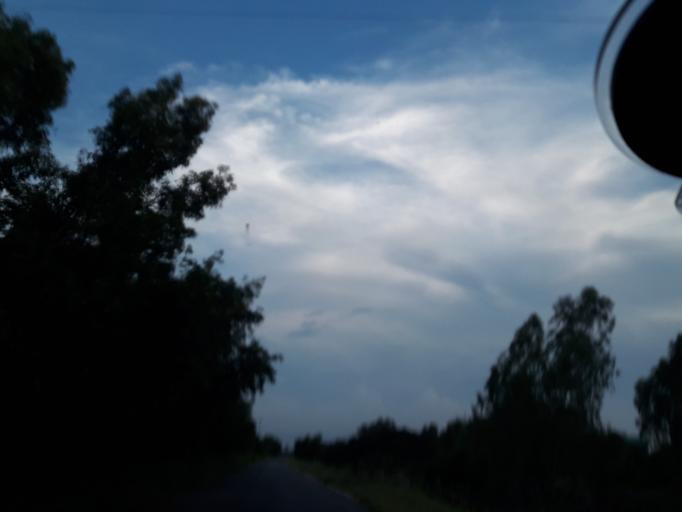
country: TH
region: Pathum Thani
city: Nong Suea
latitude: 14.2199
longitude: 100.8688
